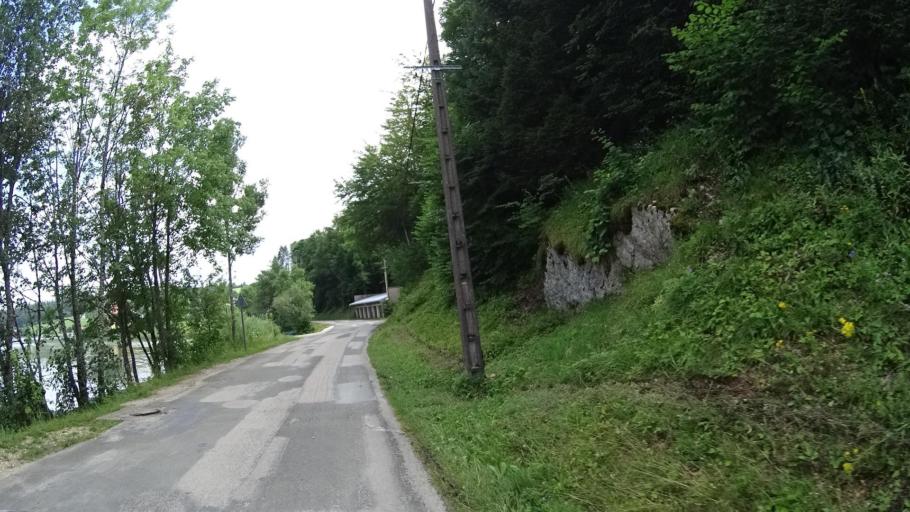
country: FR
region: Franche-Comte
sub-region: Departement du Doubs
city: Les Fourgs
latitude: 46.8315
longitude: 6.3388
